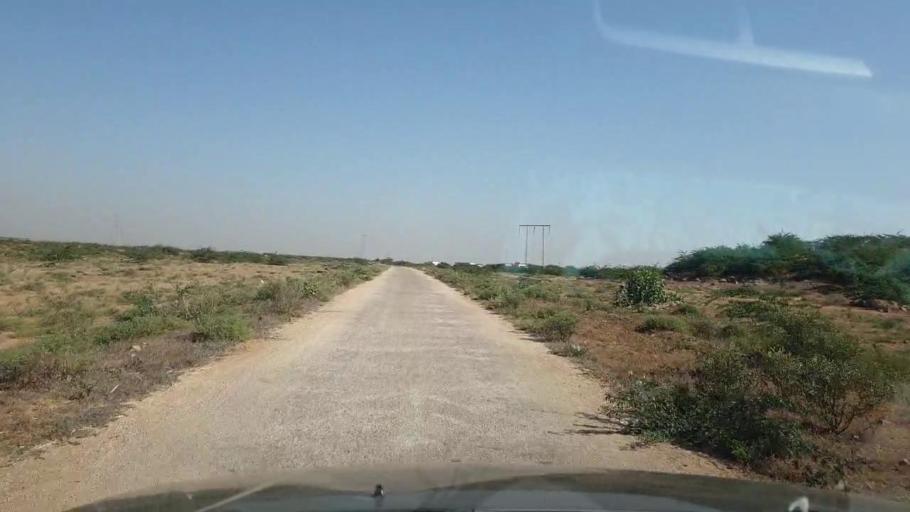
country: PK
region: Sindh
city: Thatta
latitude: 24.8621
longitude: 67.7796
